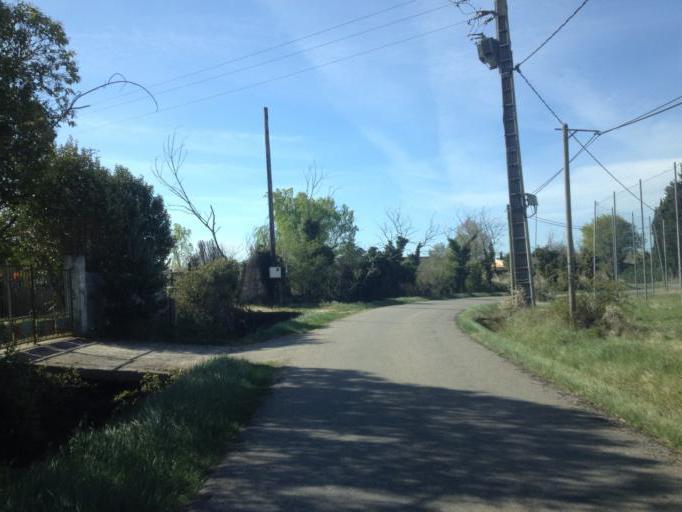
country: FR
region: Provence-Alpes-Cote d'Azur
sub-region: Departement du Vaucluse
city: Caderousse
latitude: 44.1094
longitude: 4.7559
